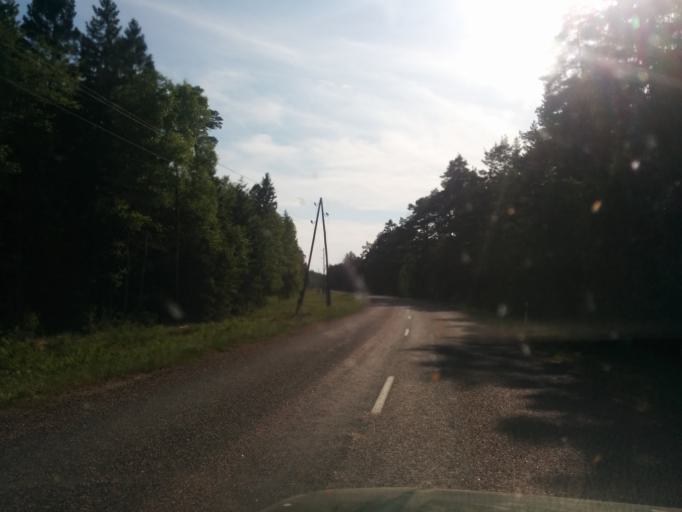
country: LV
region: Dundaga
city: Dundaga
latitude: 57.6667
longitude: 22.3075
